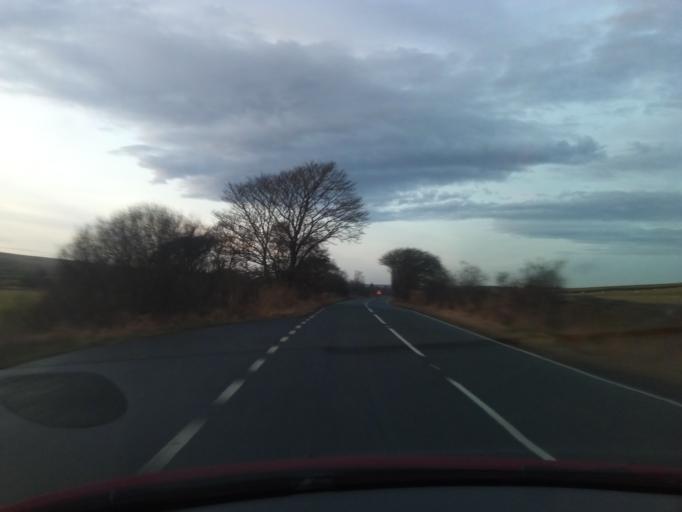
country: GB
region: England
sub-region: Northumberland
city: Otterburn
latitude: 55.2416
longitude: -2.2123
